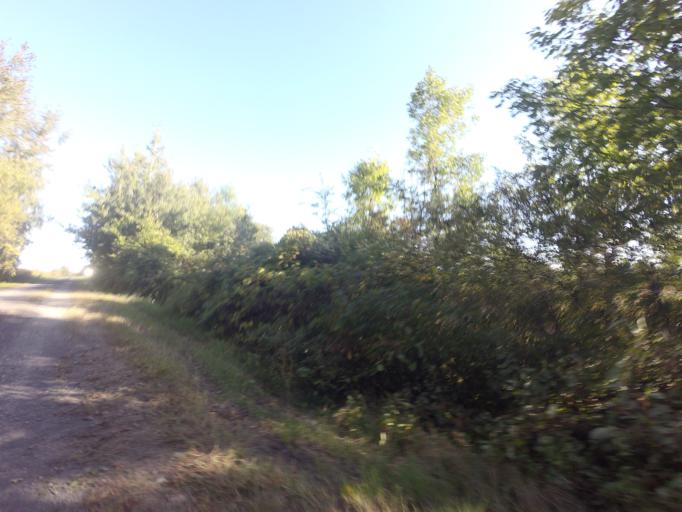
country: CA
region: Ontario
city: Hawkesbury
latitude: 45.5194
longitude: -74.5286
